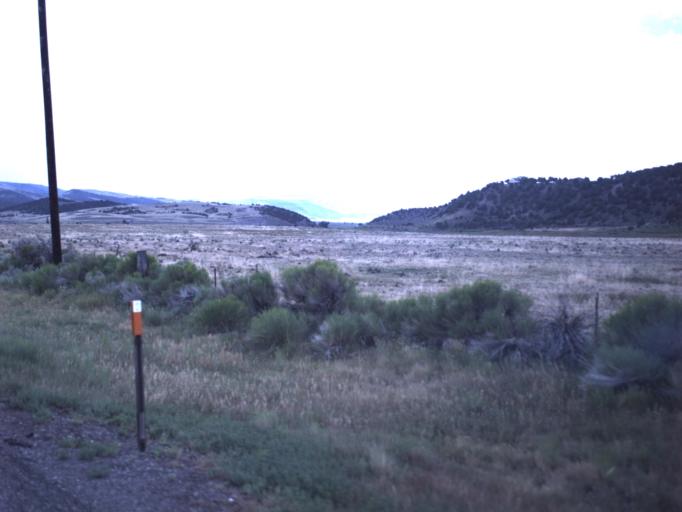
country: US
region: Utah
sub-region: Wayne County
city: Loa
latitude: 38.5850
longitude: -111.8451
